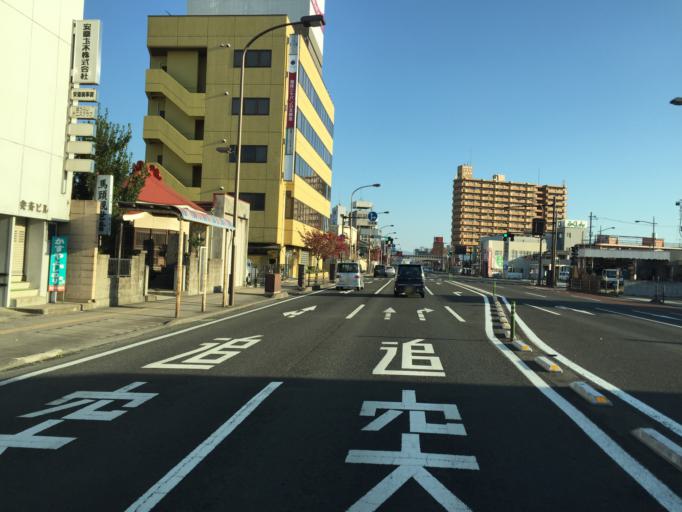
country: JP
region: Fukushima
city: Fukushima-shi
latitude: 37.7559
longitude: 140.4731
